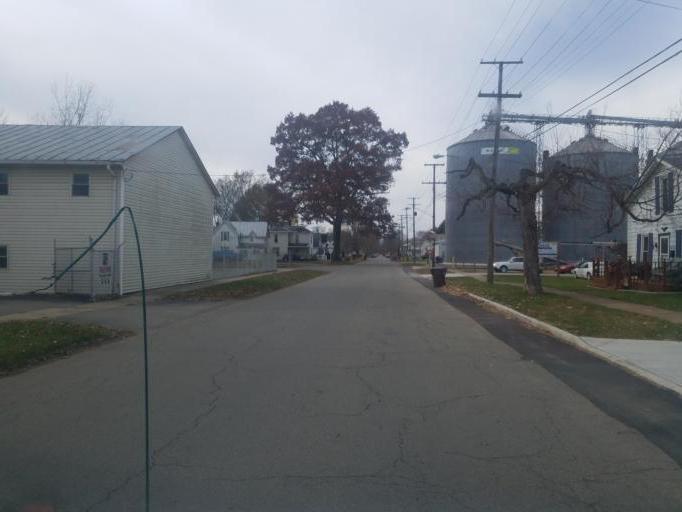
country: US
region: Ohio
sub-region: Knox County
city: Mount Vernon
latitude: 40.3921
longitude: -82.4919
